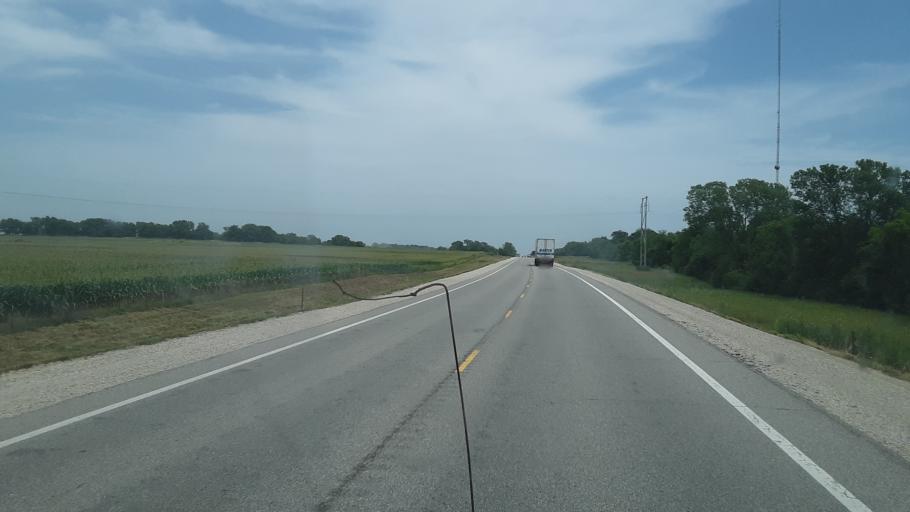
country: US
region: Kansas
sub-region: Allen County
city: Iola
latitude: 37.9109
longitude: -95.1274
